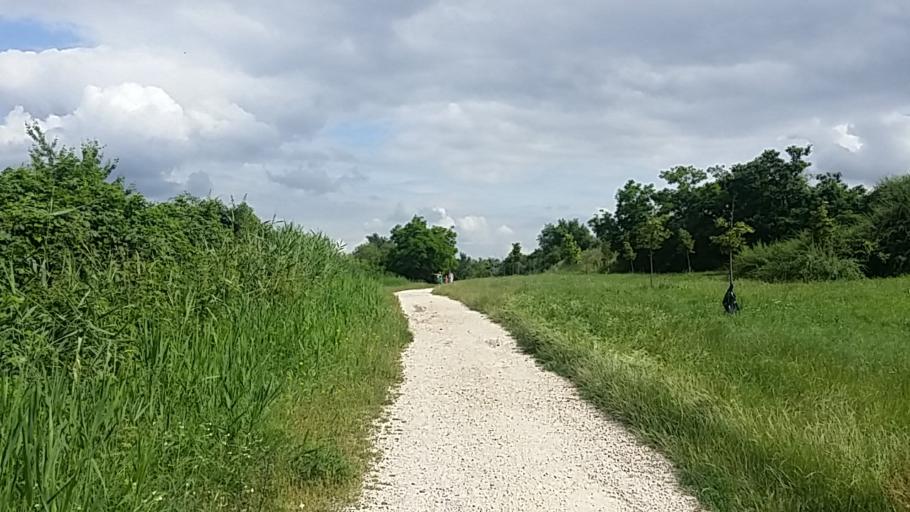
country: HU
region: Budapest
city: Budapest XX. keruelet
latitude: 47.4192
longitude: 19.0943
